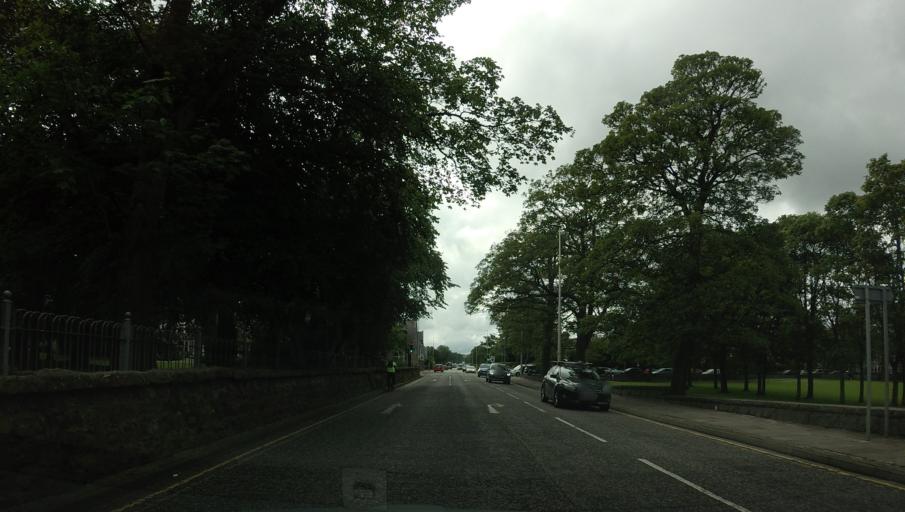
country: GB
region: Scotland
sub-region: Aberdeen City
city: Aberdeen
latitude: 57.1527
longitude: -2.1236
